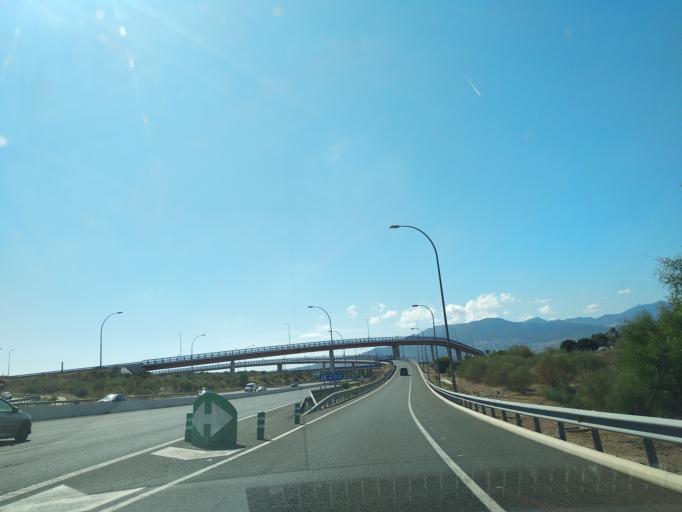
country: ES
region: Andalusia
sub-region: Provincia de Malaga
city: Alhaurin de la Torre
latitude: 36.7159
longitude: -4.5089
